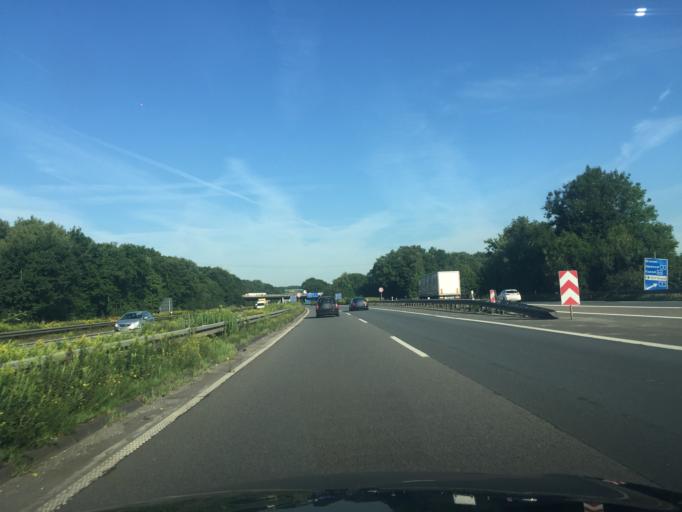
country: DE
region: North Rhine-Westphalia
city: Schwerte
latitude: 51.4306
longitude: 7.5379
